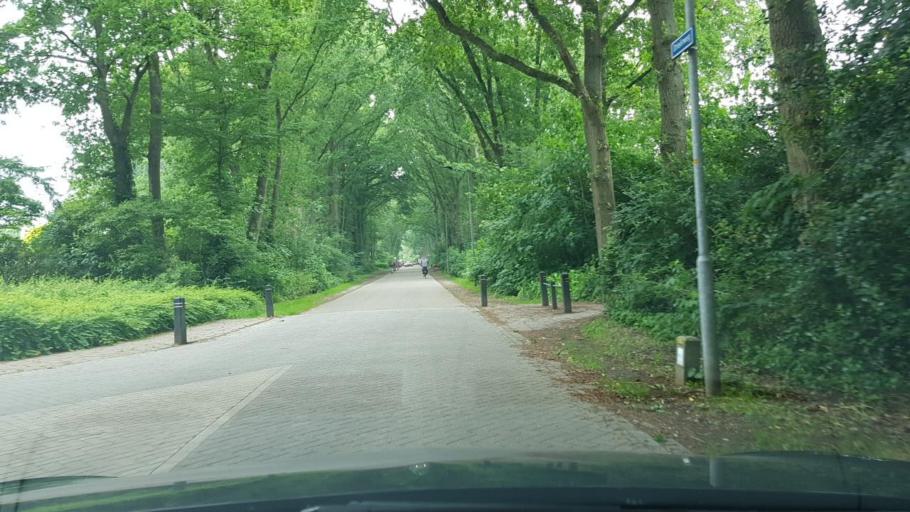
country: NL
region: Gelderland
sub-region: Gemeente Ermelo
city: Ermelo
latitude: 52.2934
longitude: 5.6390
